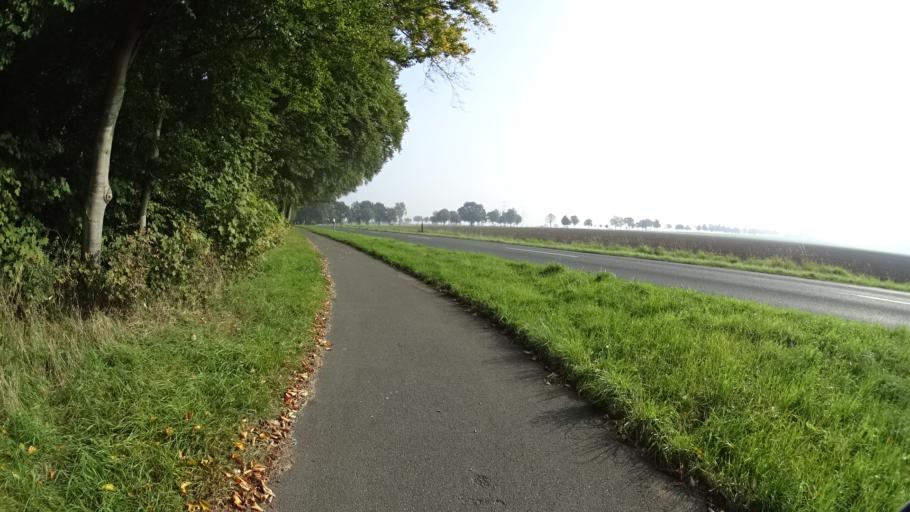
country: DE
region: Lower Saxony
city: Reppenstedt
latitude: 53.2200
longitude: 10.3537
